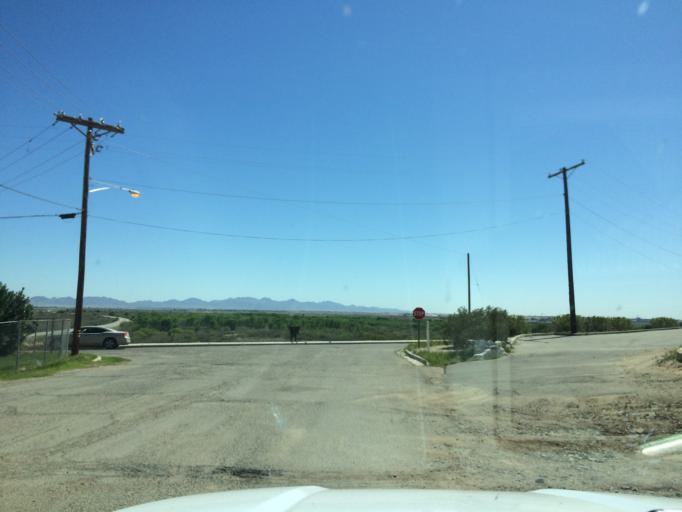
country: US
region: Arizona
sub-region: Yuma County
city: Yuma
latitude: 32.7317
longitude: -114.6157
